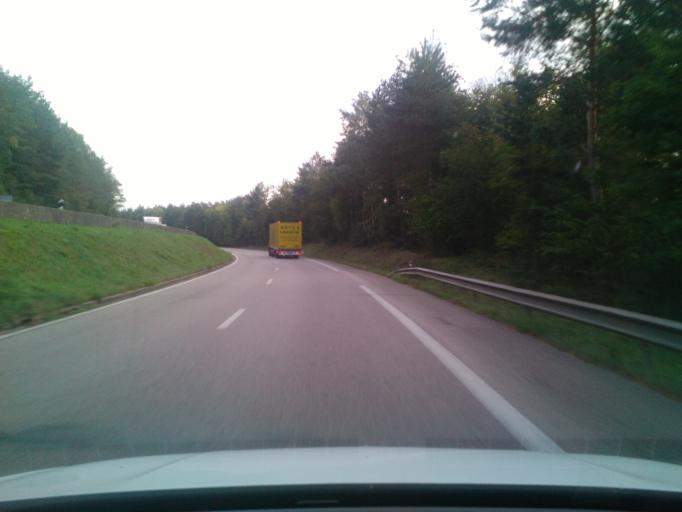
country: FR
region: Lorraine
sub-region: Departement des Vosges
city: Saint-Die-des-Vosges
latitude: 48.2709
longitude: 6.9457
